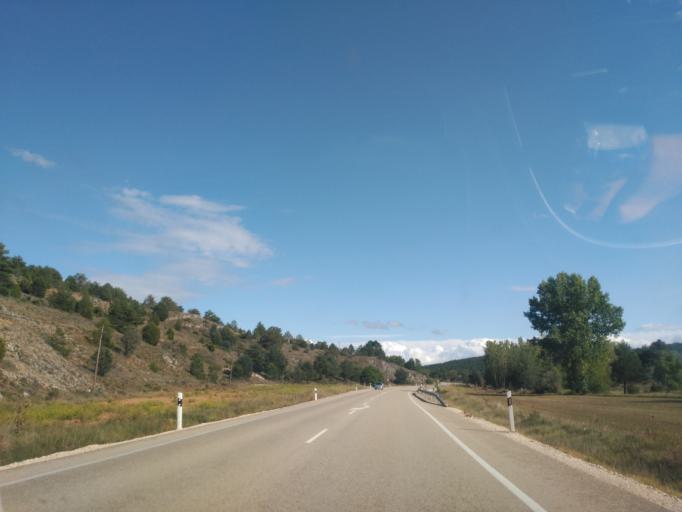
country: ES
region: Castille and Leon
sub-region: Provincia de Burgos
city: Rabanera del Pinar
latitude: 41.8720
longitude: -3.2178
